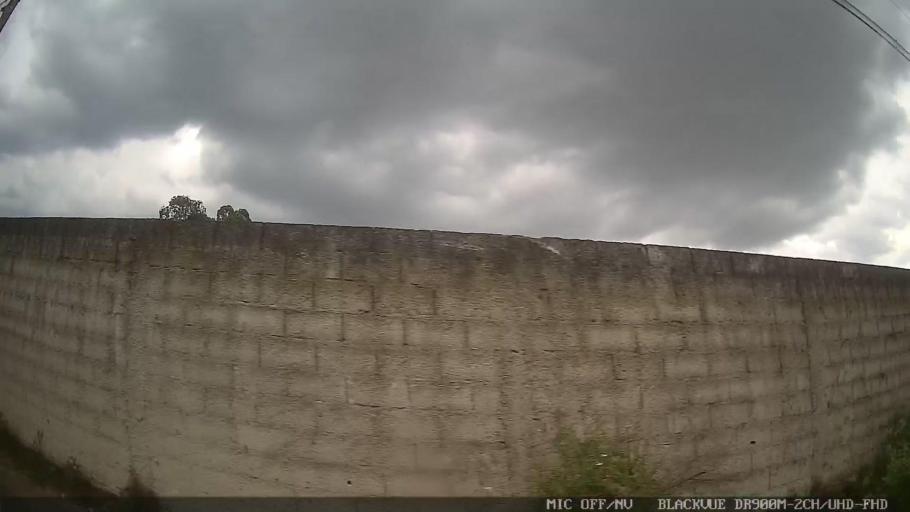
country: BR
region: Sao Paulo
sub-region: Suzano
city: Suzano
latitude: -23.5709
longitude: -46.2958
